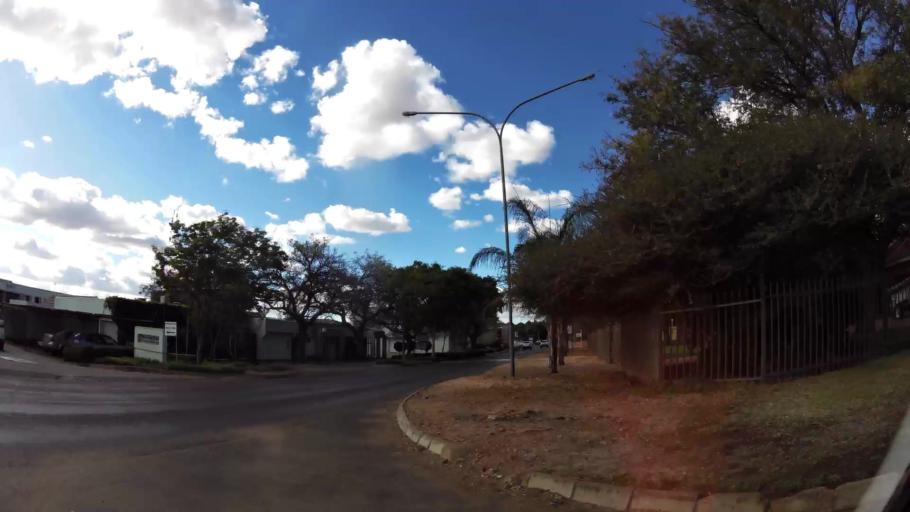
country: ZA
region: Limpopo
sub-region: Capricorn District Municipality
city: Polokwane
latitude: -23.8970
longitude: 29.4794
